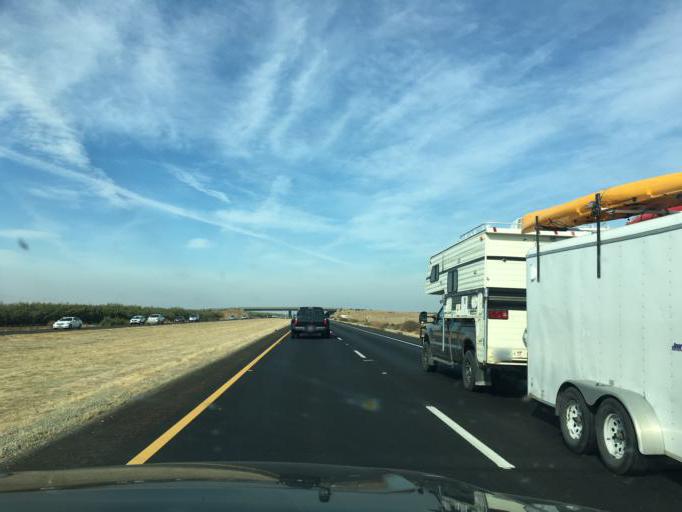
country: US
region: California
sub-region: Fresno County
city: Huron
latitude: 36.1992
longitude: -120.2091
